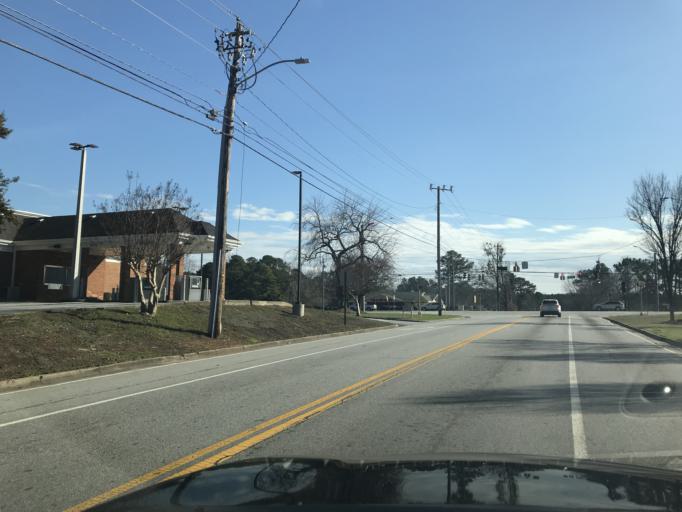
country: US
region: Georgia
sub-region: Coweta County
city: Newnan
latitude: 33.3854
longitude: -84.7846
